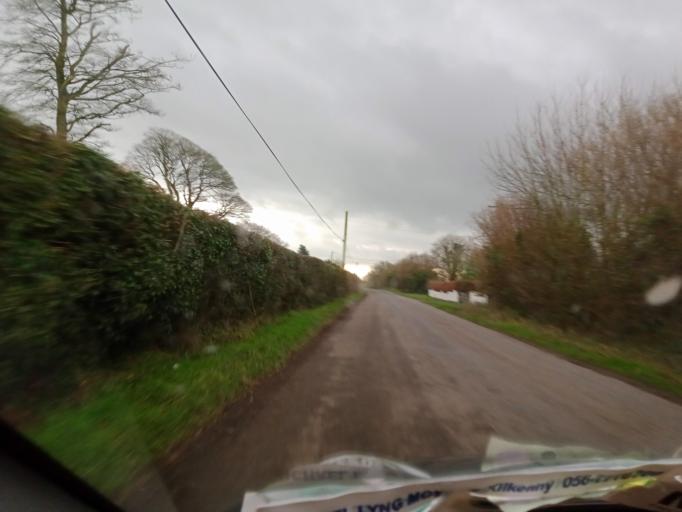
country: IE
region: Munster
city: Fethard
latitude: 52.5500
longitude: -7.7624
